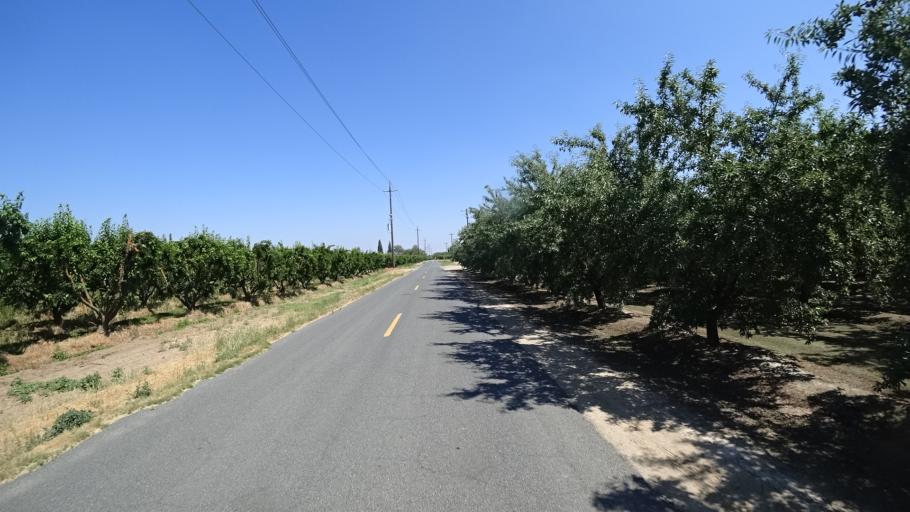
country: US
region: California
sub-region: Fresno County
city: Kingsburg
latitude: 36.4571
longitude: -119.5824
